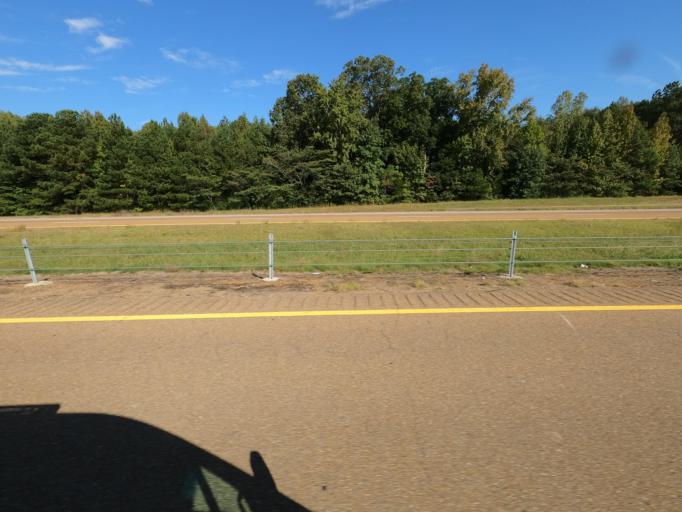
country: US
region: Tennessee
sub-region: Shelby County
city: Millington
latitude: 35.3082
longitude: -89.8182
